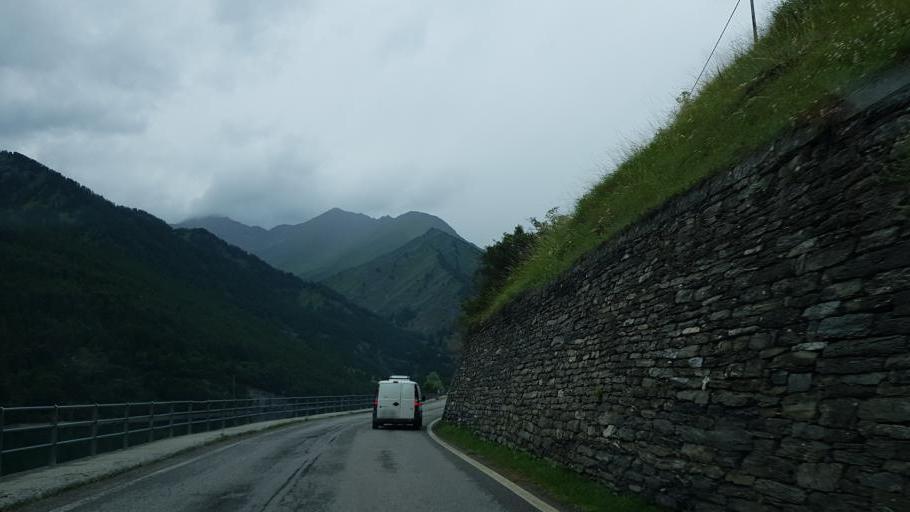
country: IT
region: Piedmont
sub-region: Provincia di Cuneo
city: Pontechianale
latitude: 44.6157
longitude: 7.0467
